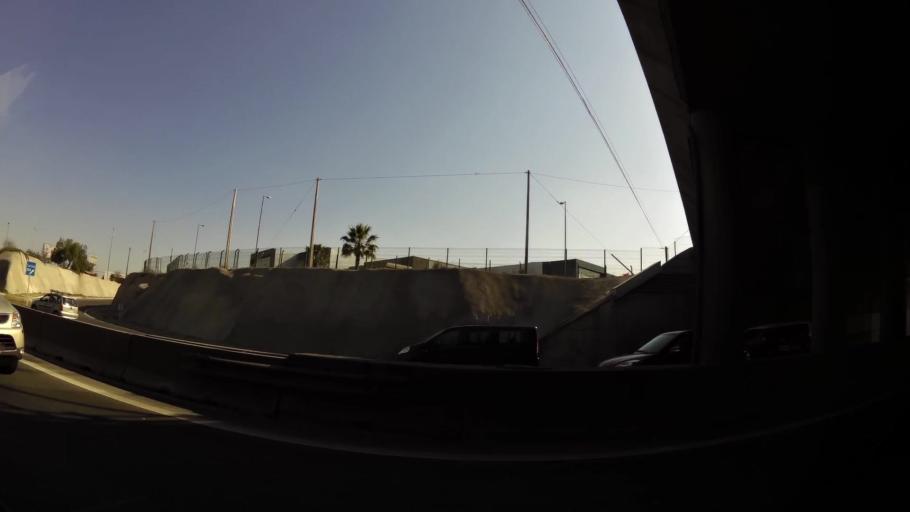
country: CL
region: Santiago Metropolitan
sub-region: Provincia de Santiago
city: Lo Prado
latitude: -33.4439
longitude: -70.7795
